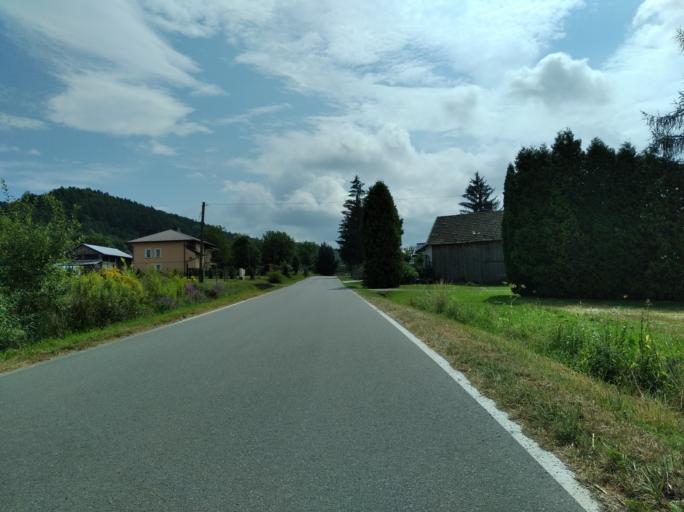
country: PL
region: Subcarpathian Voivodeship
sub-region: Powiat krosnienski
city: Wojaszowka
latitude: 49.7951
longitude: 21.6845
